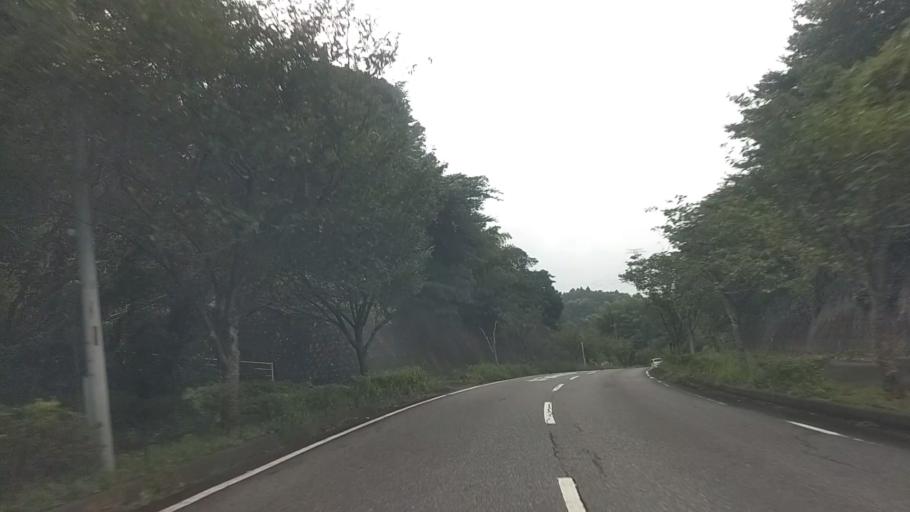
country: JP
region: Chiba
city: Kisarazu
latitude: 35.3819
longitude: 140.0078
